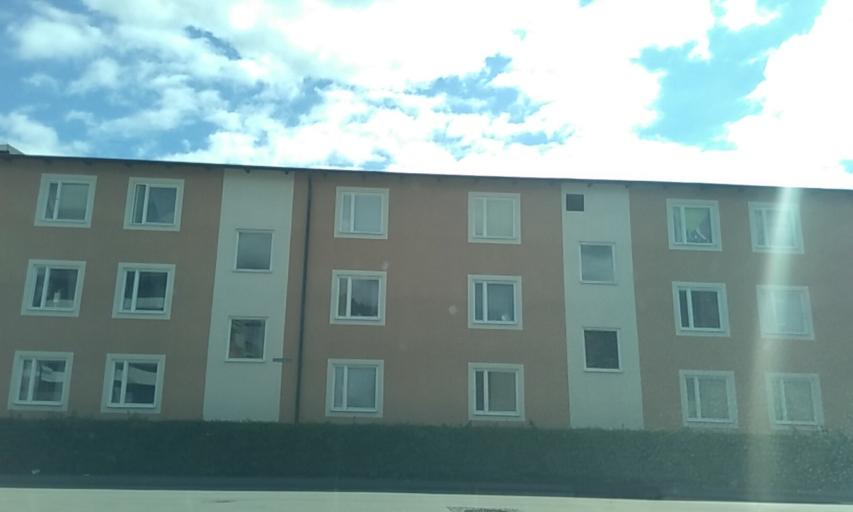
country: SE
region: Vaestra Goetaland
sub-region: Skara Kommun
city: Skara
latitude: 58.3843
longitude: 13.4425
